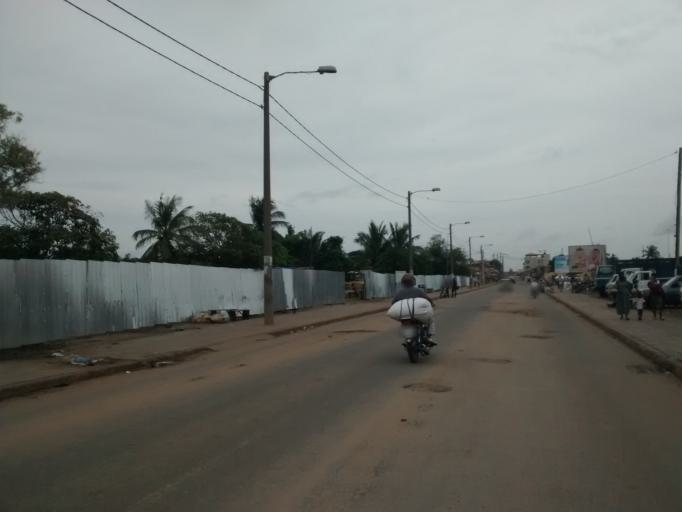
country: TG
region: Maritime
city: Lome
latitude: 6.1409
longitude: 1.2177
